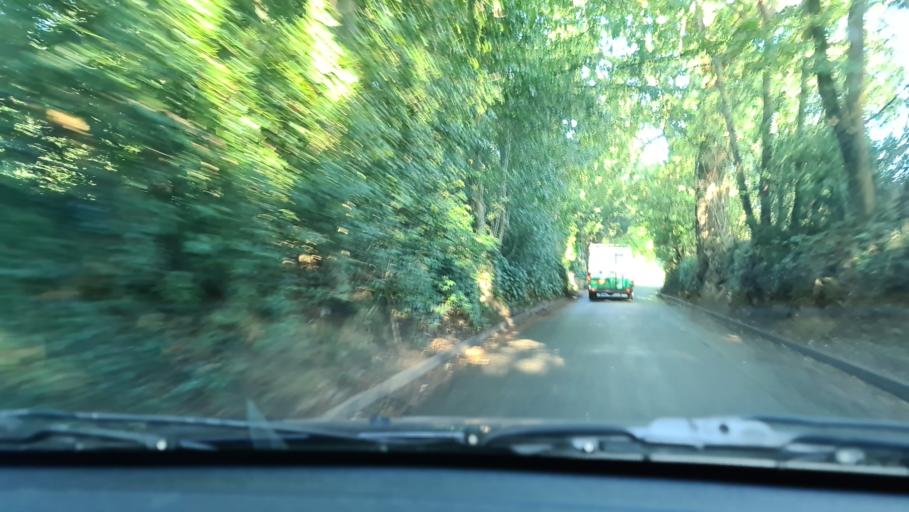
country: GB
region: England
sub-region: Hertfordshire
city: Chorleywood
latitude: 51.6405
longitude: -0.5185
